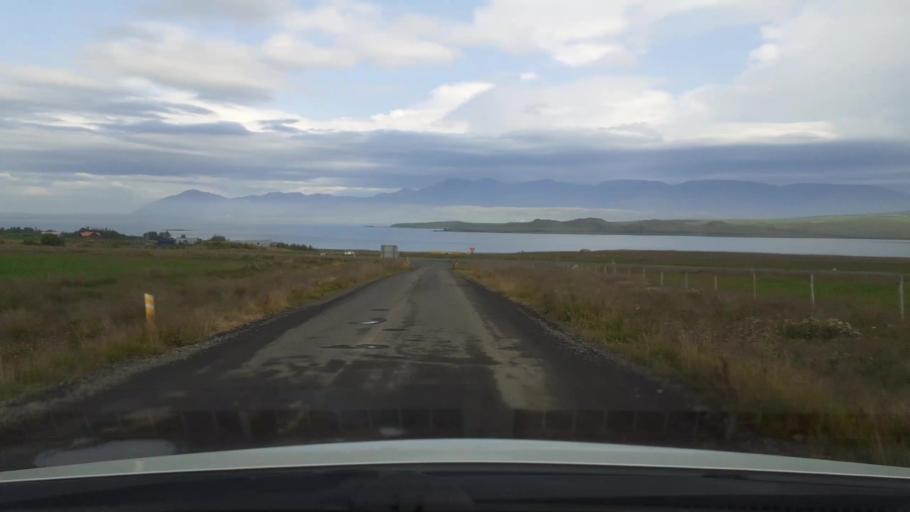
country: IS
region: Capital Region
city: Mosfellsbaer
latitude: 64.3292
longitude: -21.6537
